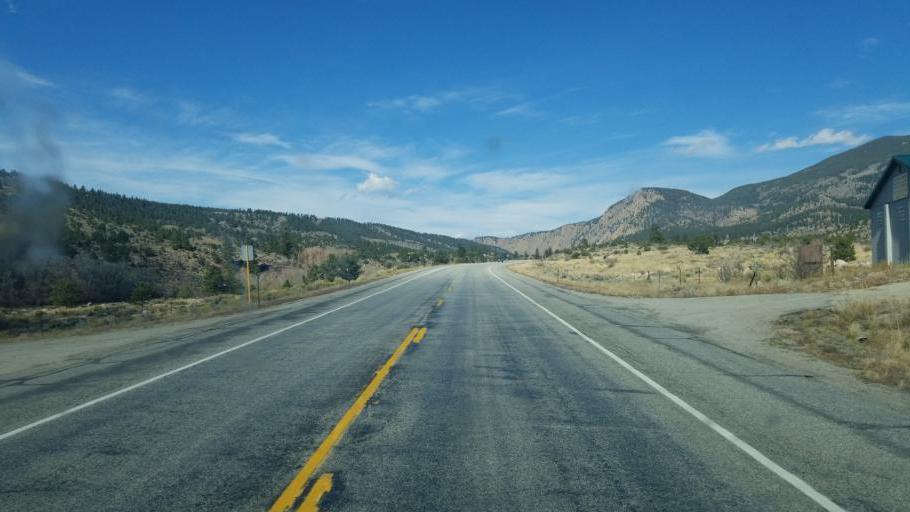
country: US
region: Colorado
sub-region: Chaffee County
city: Buena Vista
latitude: 38.9620
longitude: -106.2038
